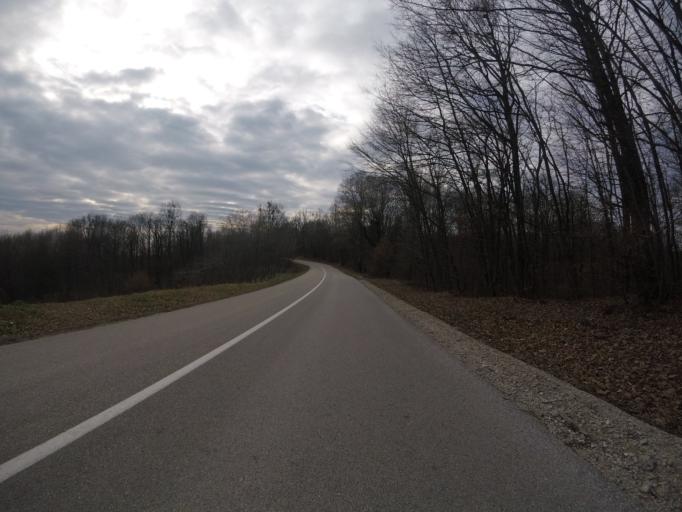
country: HR
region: Zagrebacka
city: Mraclin
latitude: 45.5340
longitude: 16.0572
